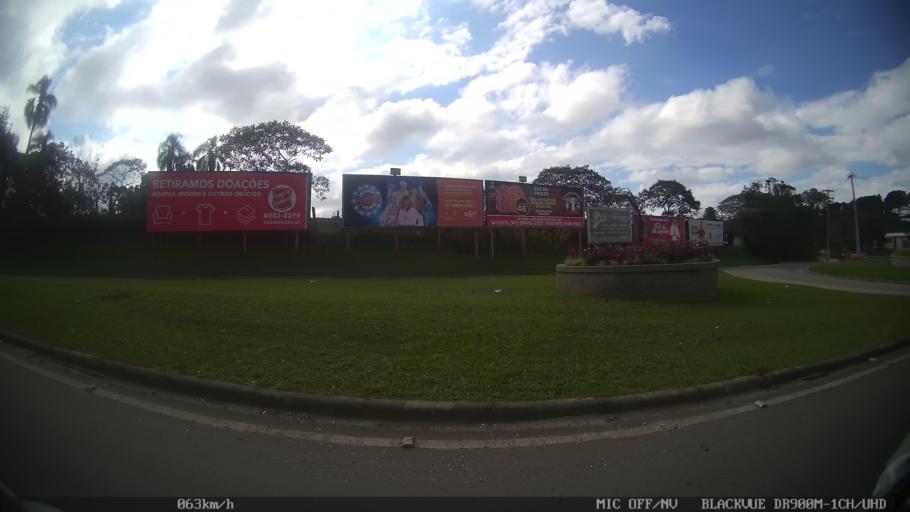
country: BR
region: Parana
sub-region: Colombo
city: Colombo
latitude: -25.3433
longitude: -49.1863
